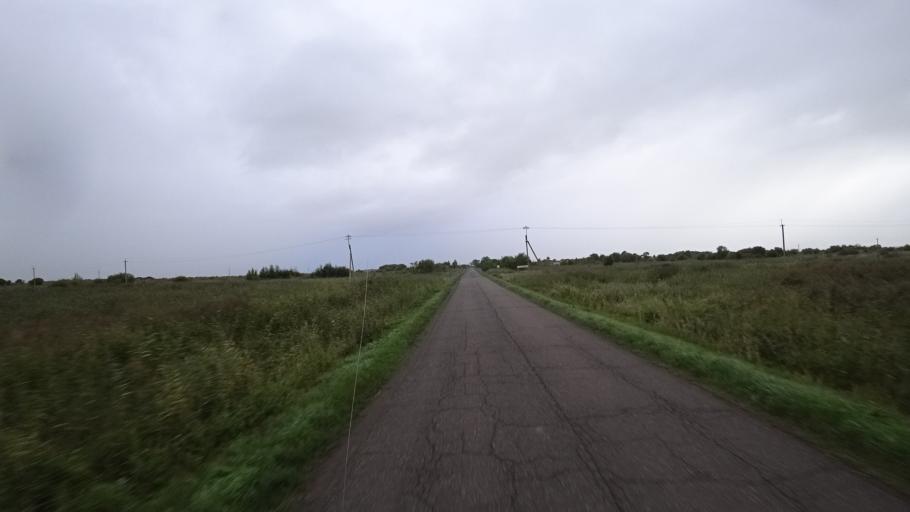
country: RU
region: Primorskiy
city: Chernigovka
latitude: 44.3937
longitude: 132.5285
